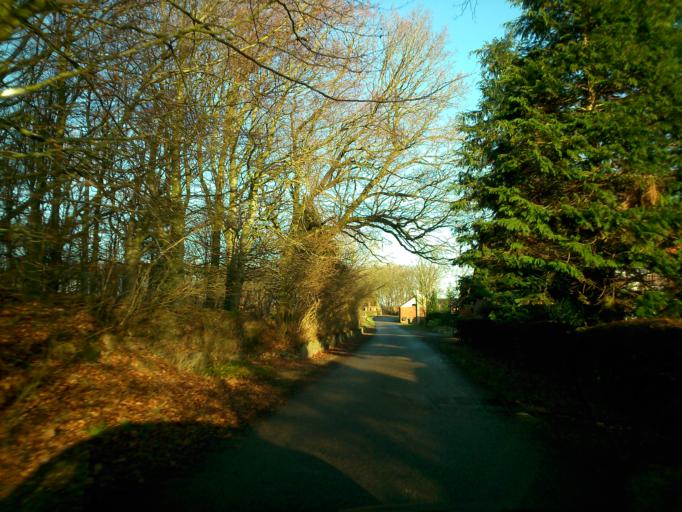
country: DK
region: Central Jutland
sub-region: Ringkobing-Skjern Kommune
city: Skjern
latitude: 55.9780
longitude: 8.5668
